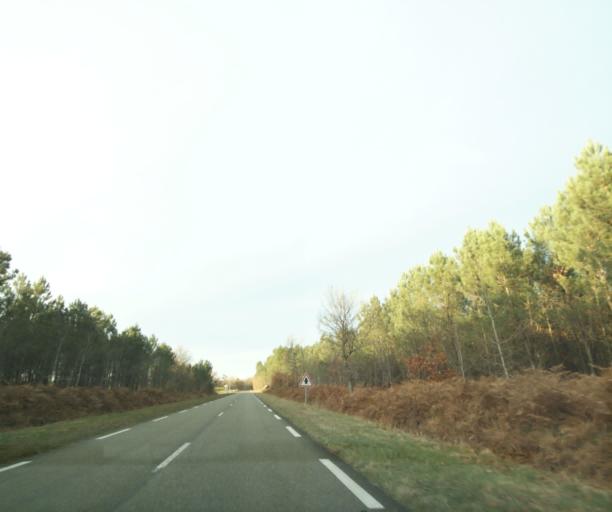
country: FR
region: Aquitaine
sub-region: Departement de la Gironde
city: Grignols
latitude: 44.1882
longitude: -0.1514
